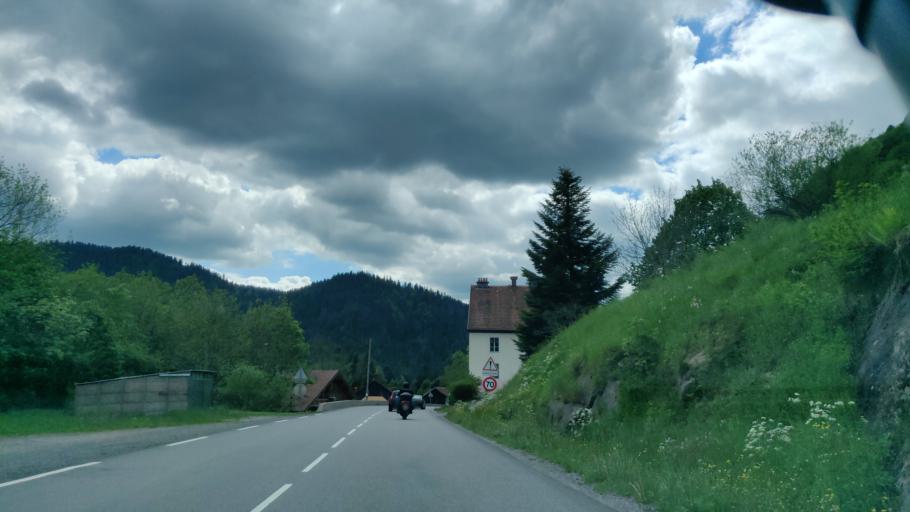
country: FR
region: Lorraine
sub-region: Departement des Vosges
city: La Bresse
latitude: 48.0035
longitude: 6.9281
